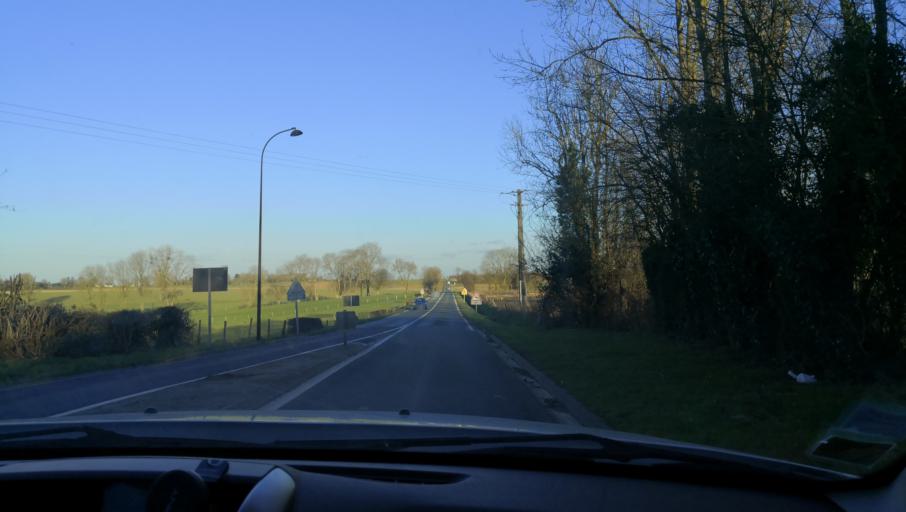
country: FR
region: Haute-Normandie
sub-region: Departement de la Seine-Maritime
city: Buchy
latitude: 49.5928
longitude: 1.4140
